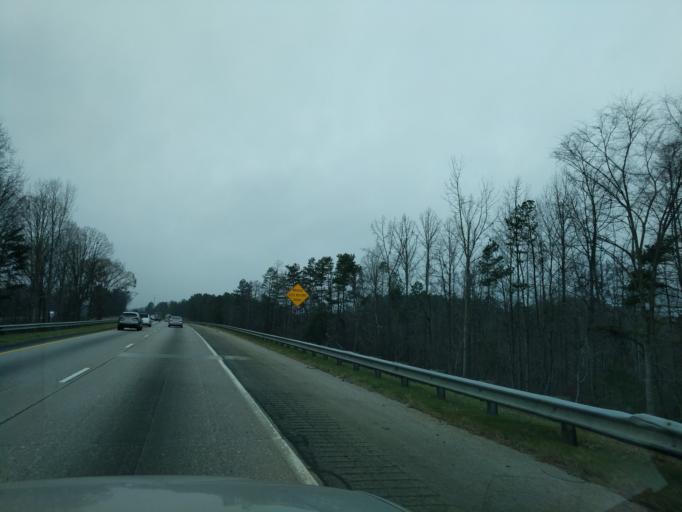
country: US
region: Georgia
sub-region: Jackson County
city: Commerce
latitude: 34.2840
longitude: -83.4277
